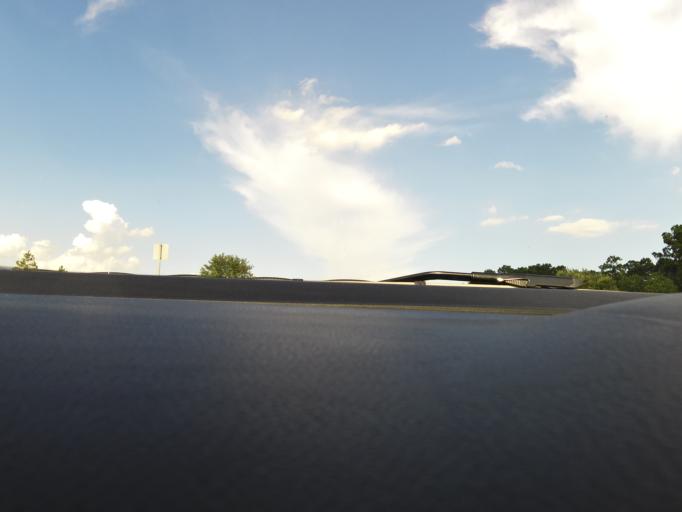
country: US
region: Texas
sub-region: Harris County
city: Aldine
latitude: 29.9686
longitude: -95.3352
